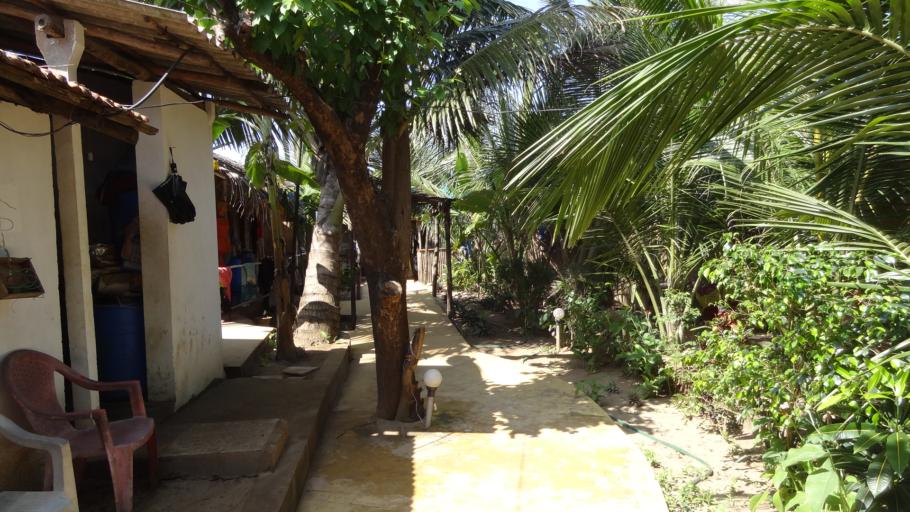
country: IN
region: Goa
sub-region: North Goa
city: Morjim
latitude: 15.6503
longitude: 73.7164
